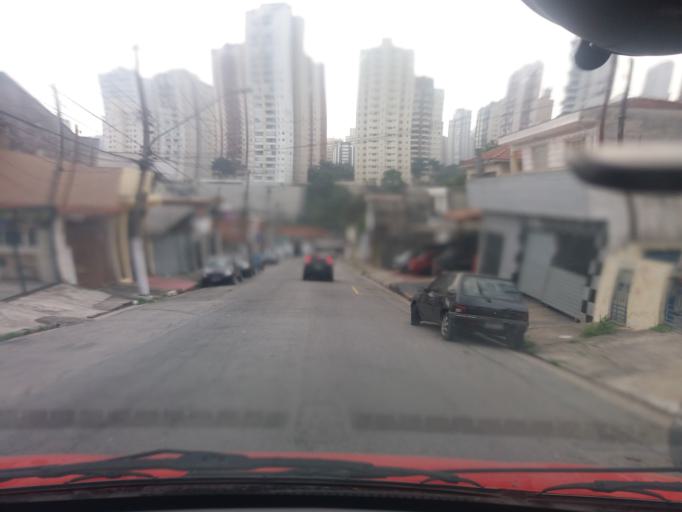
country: BR
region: Sao Paulo
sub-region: Taboao Da Serra
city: Taboao da Serra
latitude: -23.6183
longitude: -46.7452
